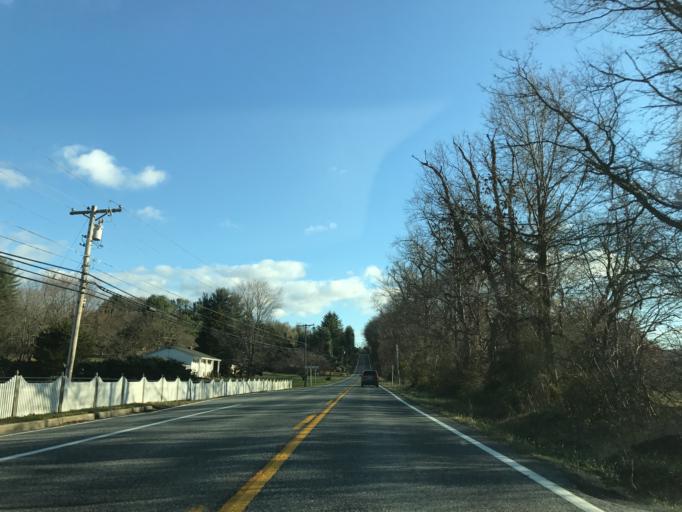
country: US
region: Maryland
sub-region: Harford County
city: Jarrettsville
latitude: 39.5867
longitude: -76.5055
